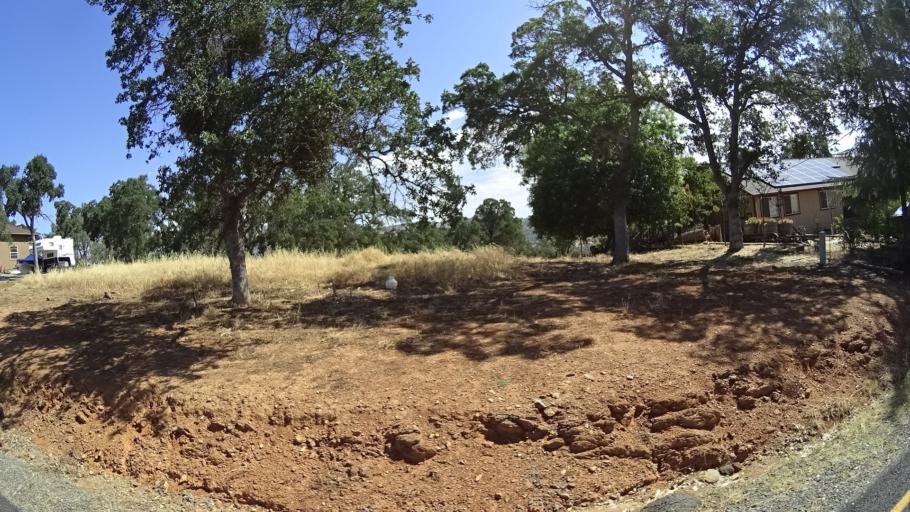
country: US
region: California
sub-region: Calaveras County
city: Copperopolis
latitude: 37.9199
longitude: -120.6232
